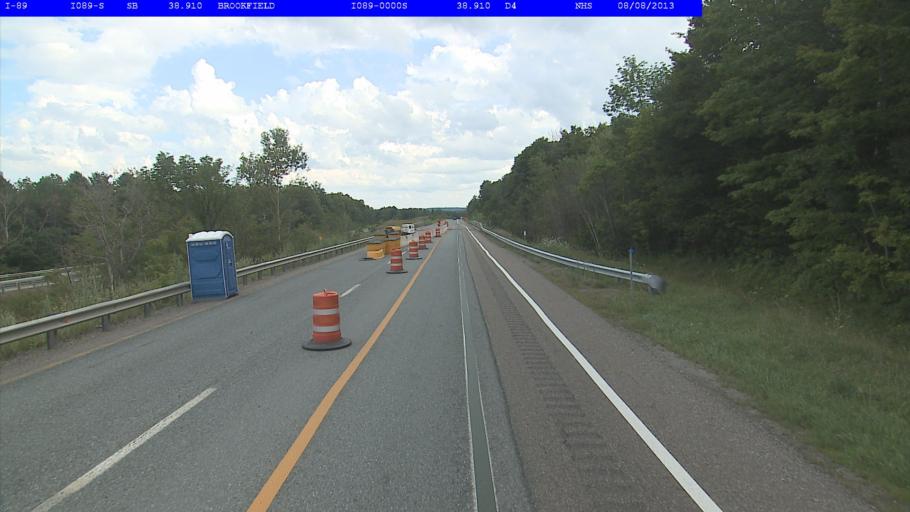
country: US
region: Vermont
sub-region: Orange County
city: Williamstown
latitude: 44.0585
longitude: -72.6061
